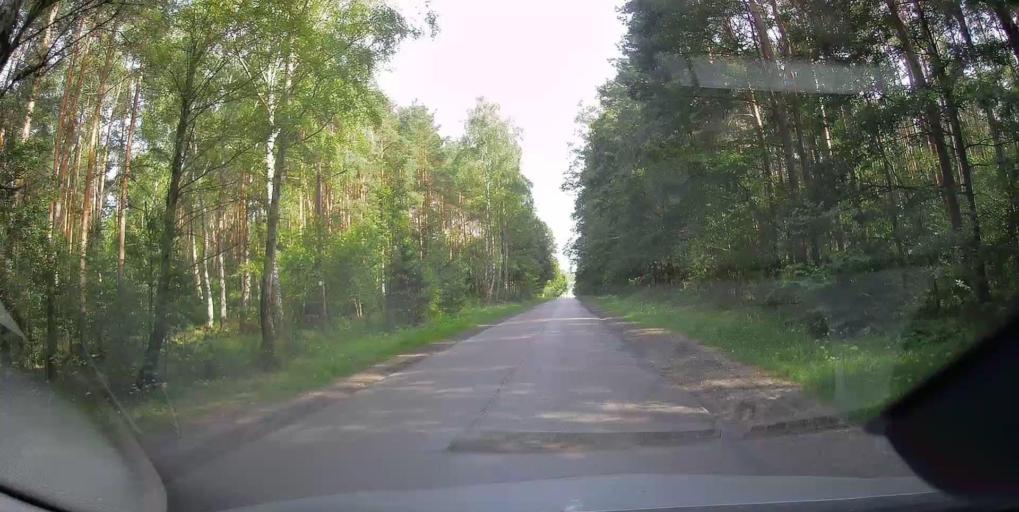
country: PL
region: Lodz Voivodeship
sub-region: Powiat tomaszowski
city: Tomaszow Mazowiecki
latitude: 51.4649
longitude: 20.0282
